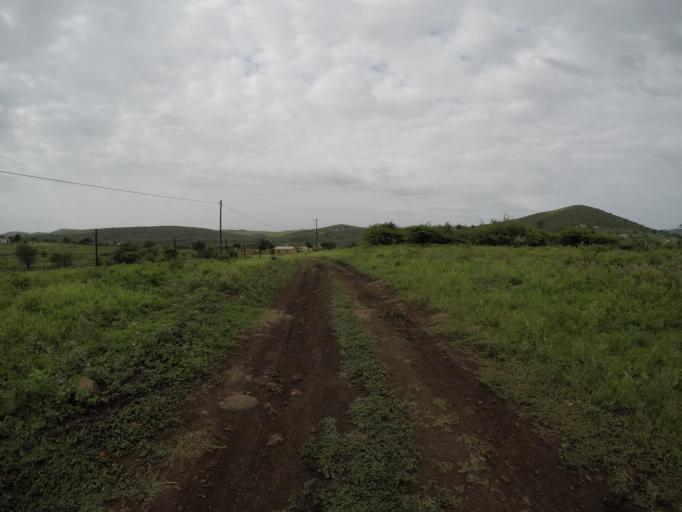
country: ZA
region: KwaZulu-Natal
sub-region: uThungulu District Municipality
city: Empangeni
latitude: -28.6387
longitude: 31.9039
